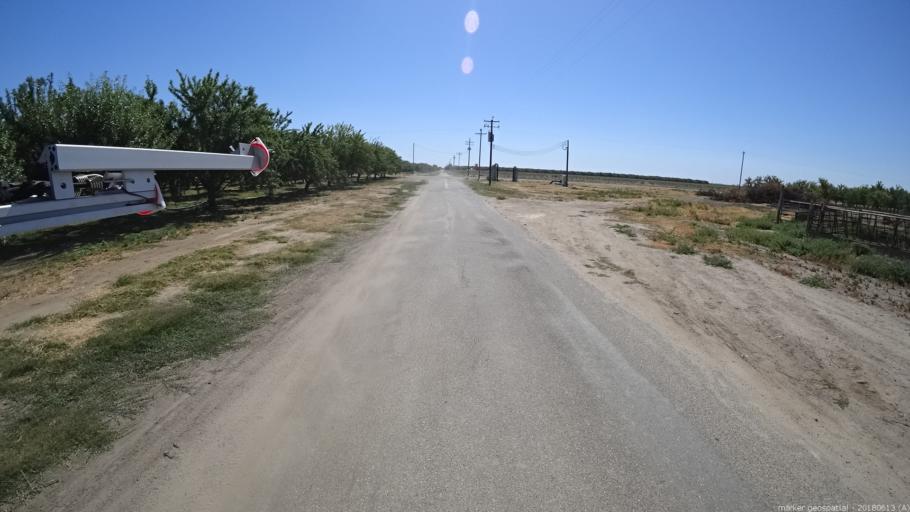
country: US
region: California
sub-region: Madera County
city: Chowchilla
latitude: 37.0762
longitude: -120.4381
